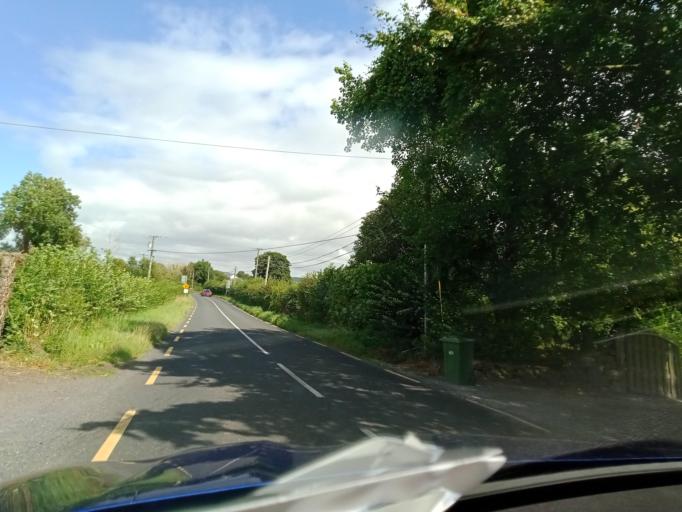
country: IE
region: Leinster
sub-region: Laois
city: Abbeyleix
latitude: 52.9292
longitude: -7.3260
